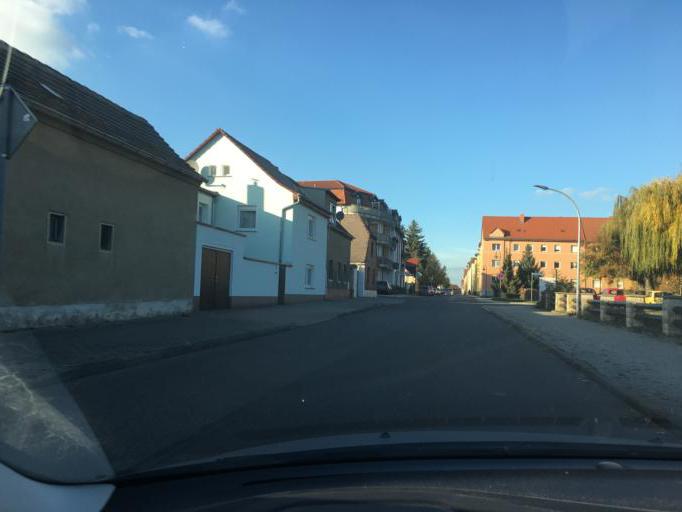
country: DE
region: Saxony-Anhalt
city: Lutzen
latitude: 51.2557
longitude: 12.1461
